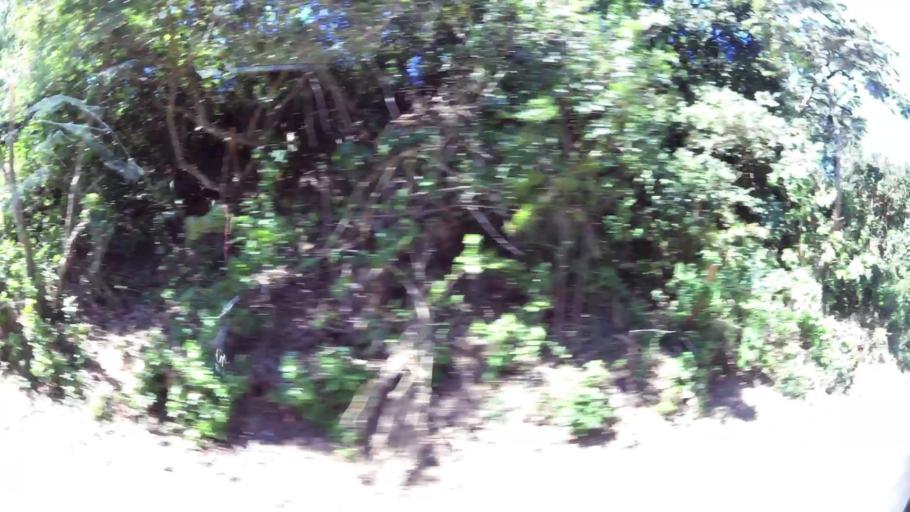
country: SV
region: Sonsonate
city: Juayua
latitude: 13.8443
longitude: -89.7656
